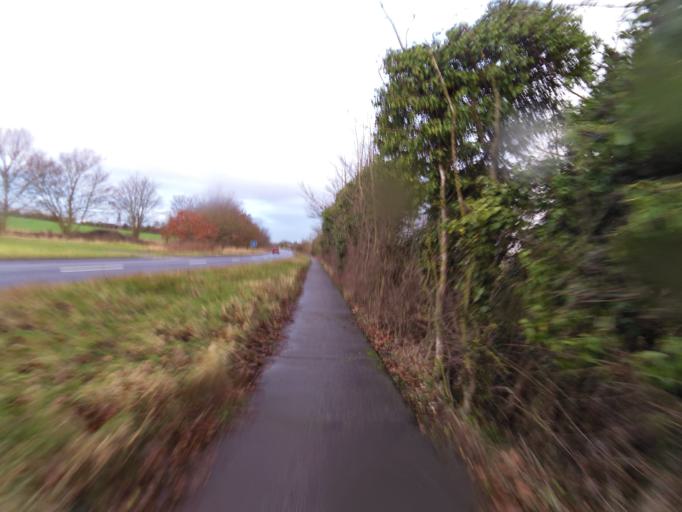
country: GB
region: England
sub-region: Suffolk
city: Needham Market
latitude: 52.1702
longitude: 1.0259
